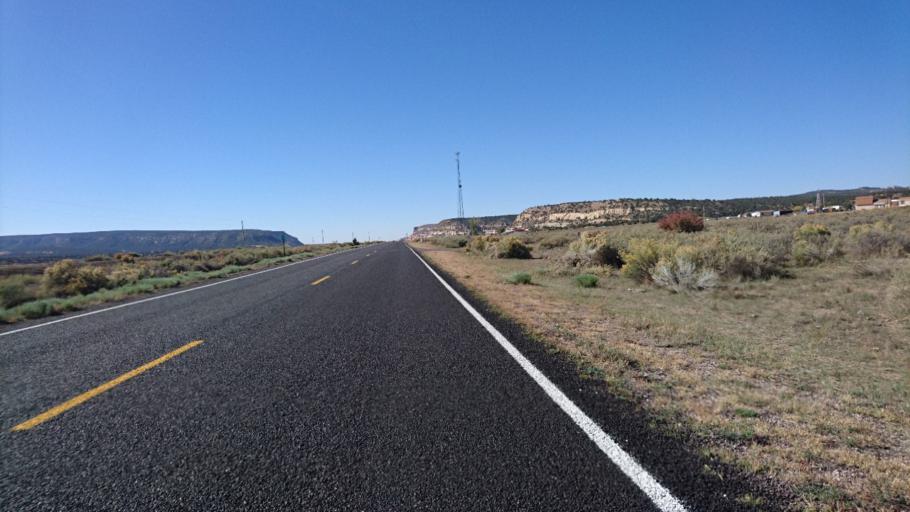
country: US
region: Arizona
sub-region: Apache County
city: Houck
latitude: 35.3982
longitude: -109.0164
